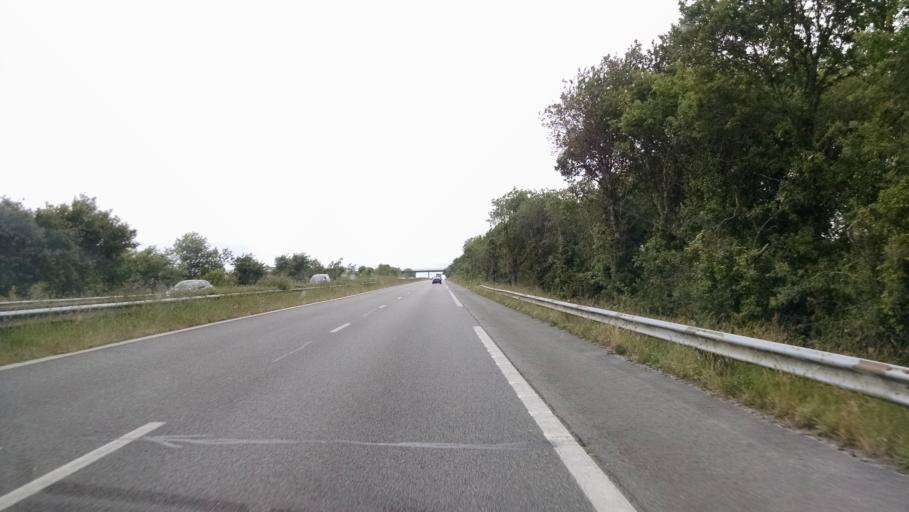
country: FR
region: Brittany
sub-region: Departement du Finistere
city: Le Trevoux
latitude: 47.8794
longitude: -3.6676
